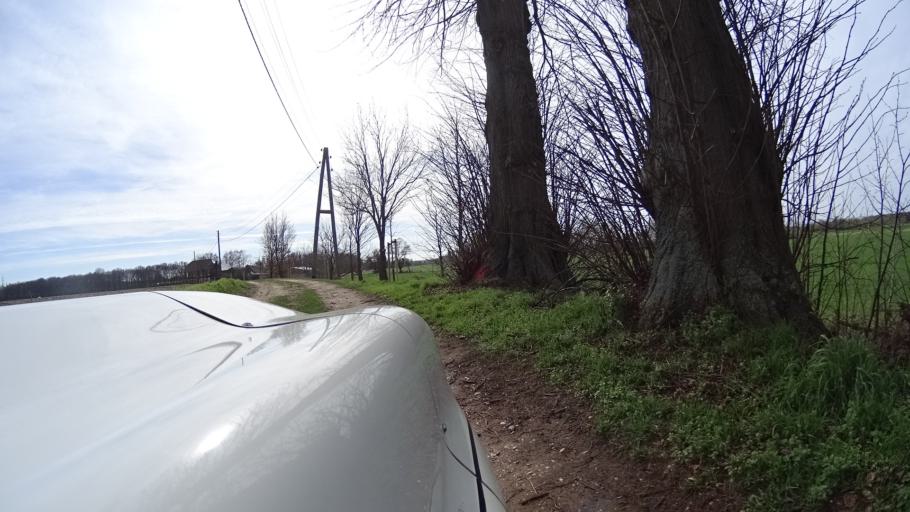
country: DE
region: North Rhine-Westphalia
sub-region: Regierungsbezirk Dusseldorf
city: Kevelaer
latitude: 51.6030
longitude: 6.2468
